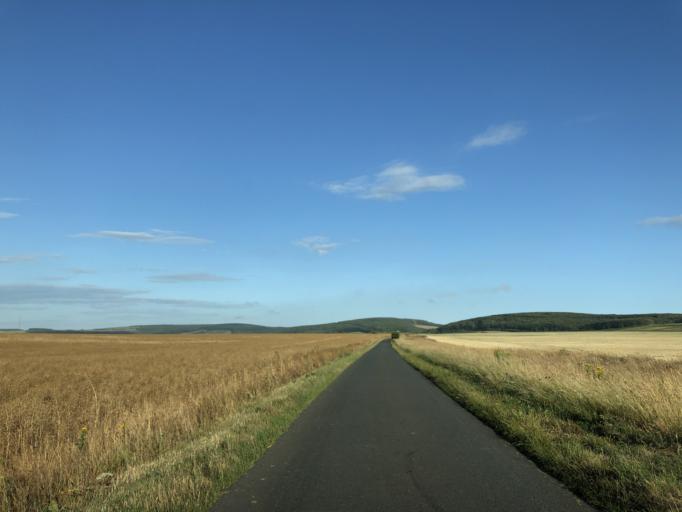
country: GB
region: England
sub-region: Isle of Wight
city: Yarmouth
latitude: 50.6816
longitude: -1.4654
